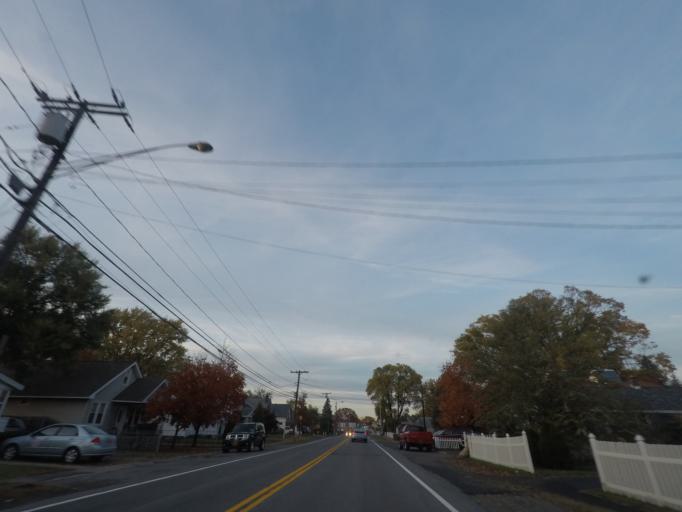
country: US
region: New York
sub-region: Schenectady County
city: Rotterdam
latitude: 42.7845
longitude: -73.9710
